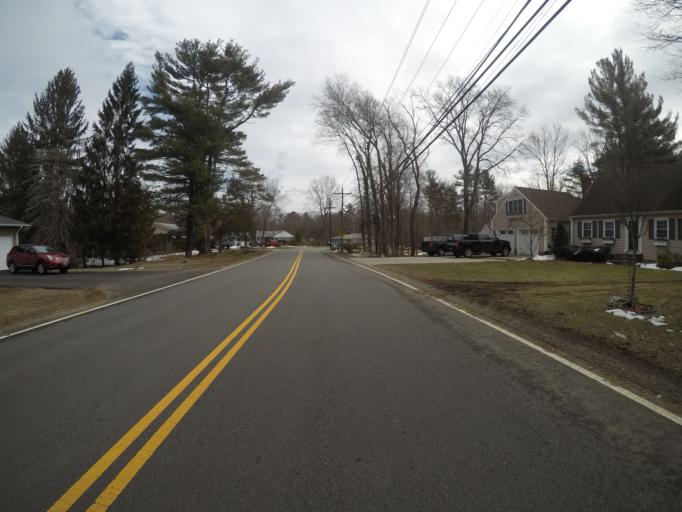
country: US
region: Massachusetts
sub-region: Bristol County
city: Easton
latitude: 42.0444
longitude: -71.0978
